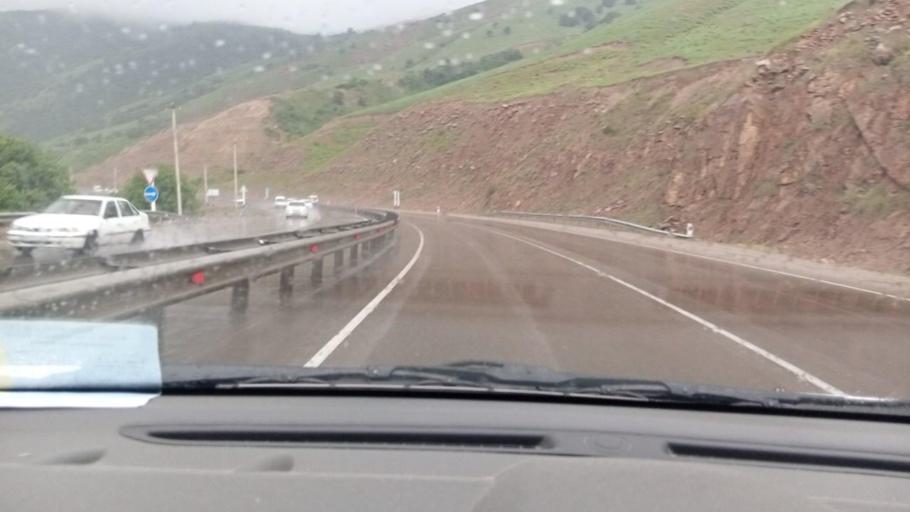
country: UZ
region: Toshkent
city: Angren
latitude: 41.0994
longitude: 70.3245
